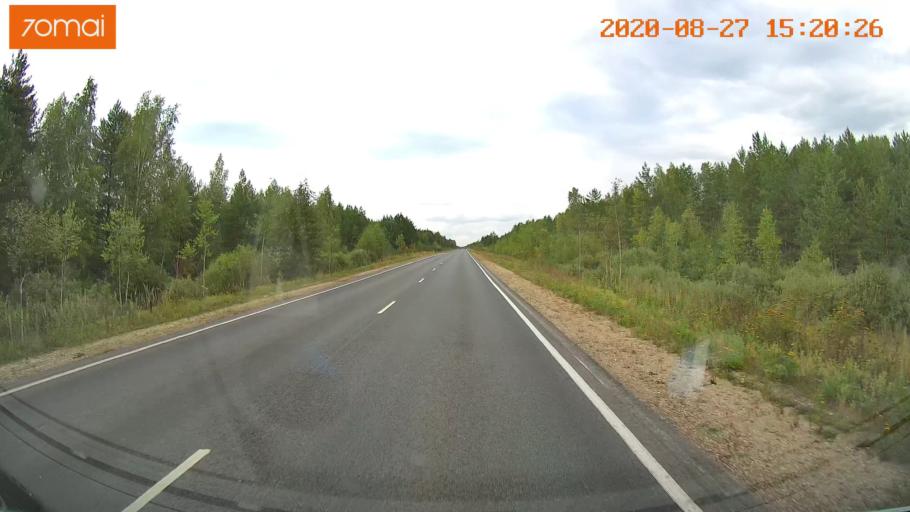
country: RU
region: Vladimir
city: Gus'-Khrustal'nyy
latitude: 55.6151
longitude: 40.7219
